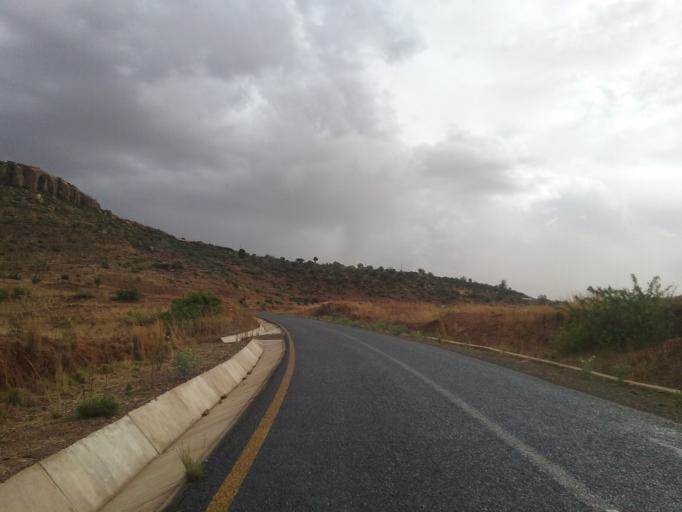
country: LS
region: Quthing
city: Quthing
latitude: -30.3682
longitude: 27.7135
